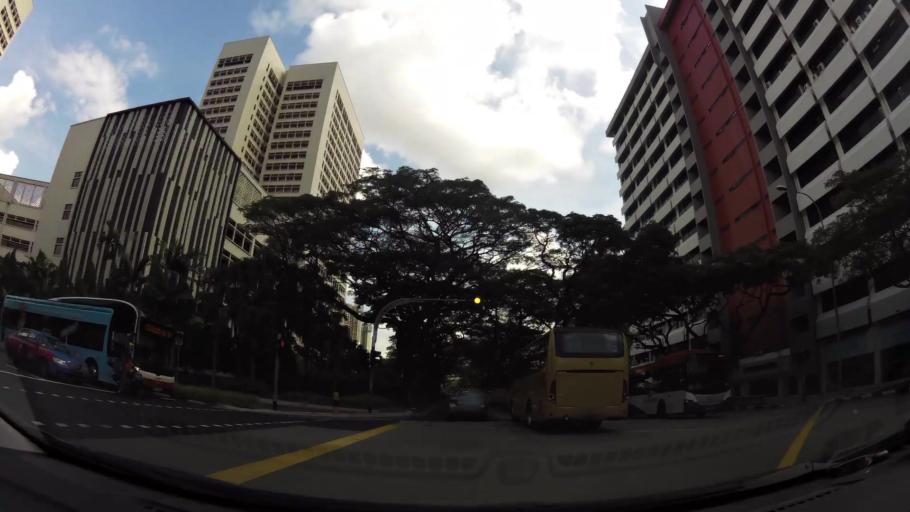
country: SG
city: Singapore
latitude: 1.2819
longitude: 103.8190
